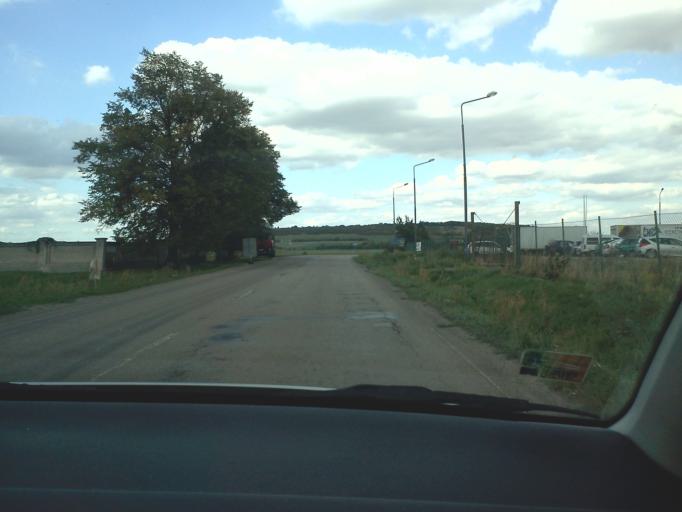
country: CZ
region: Central Bohemia
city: Prerov nad Labem
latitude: 50.1466
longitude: 14.8461
